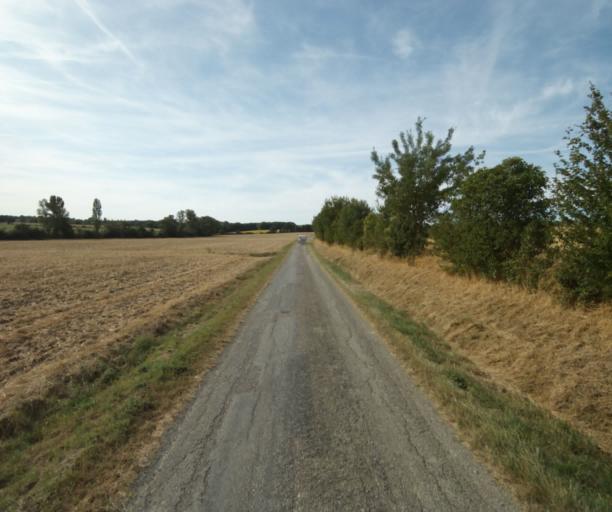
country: FR
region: Midi-Pyrenees
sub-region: Departement du Tarn
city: Puylaurens
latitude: 43.5263
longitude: 2.0390
